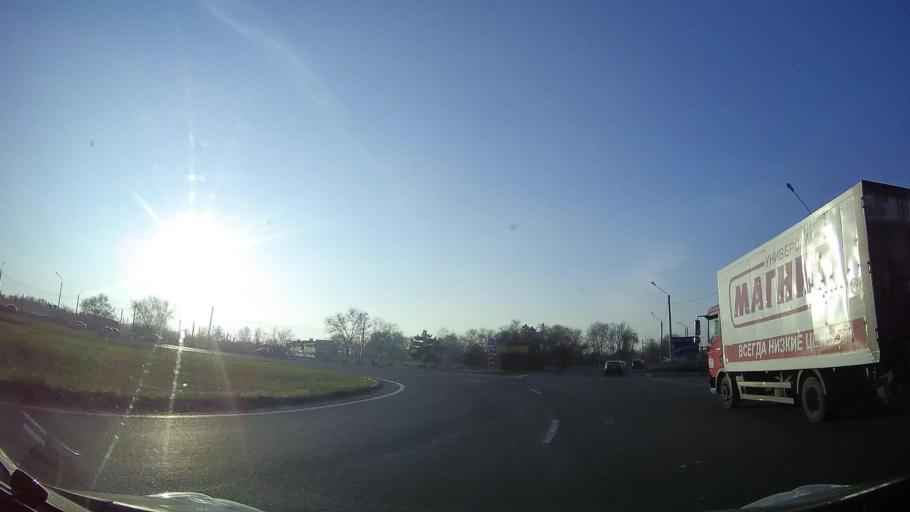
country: RU
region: Rostov
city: Bataysk
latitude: 47.0818
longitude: 39.7742
